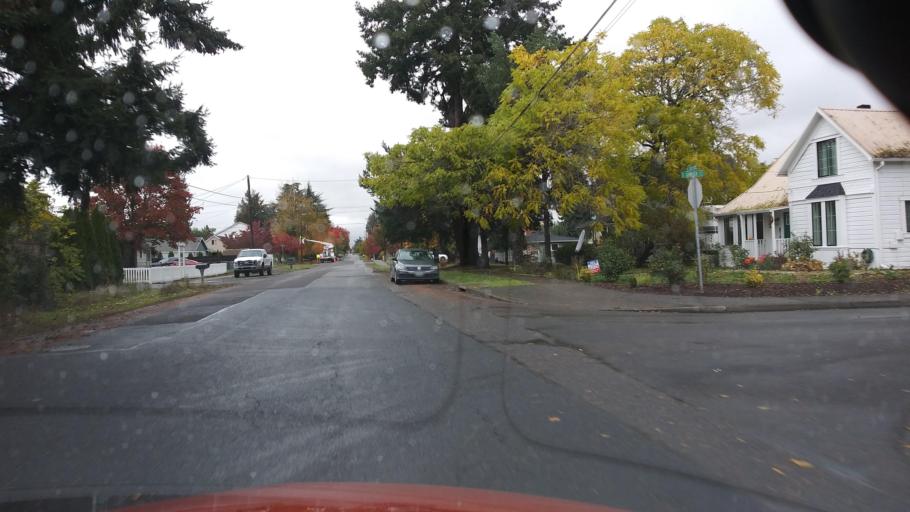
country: US
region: Oregon
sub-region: Washington County
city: Cornelius
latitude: 45.5142
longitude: -123.0570
